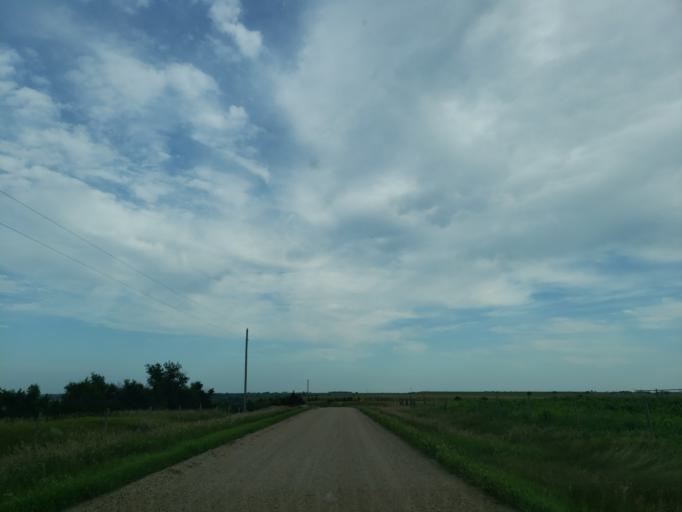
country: US
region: South Dakota
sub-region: Davison County
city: Mitchell
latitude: 43.6860
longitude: -97.9709
